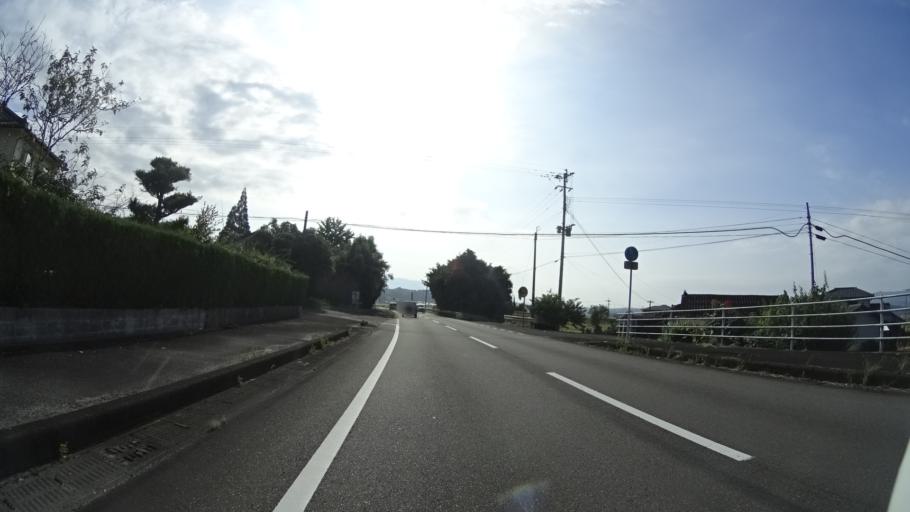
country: JP
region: Kagoshima
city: Okuchi-shinohara
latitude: 32.0163
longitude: 130.6291
